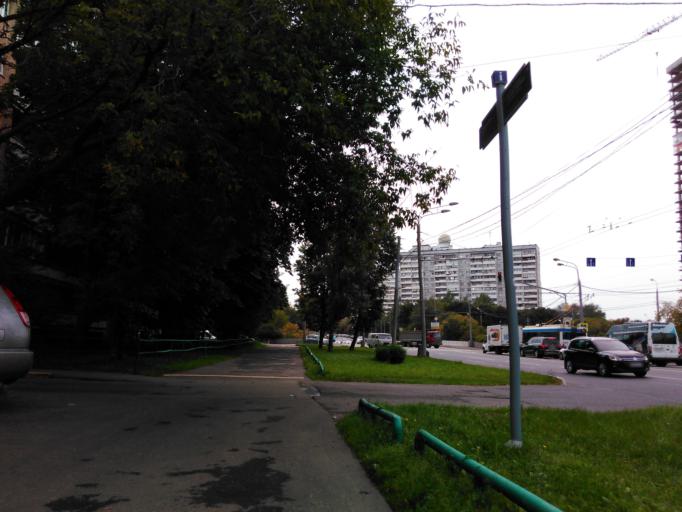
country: RU
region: Moskovskaya
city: Kastanayevo
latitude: 55.7111
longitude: 37.5079
